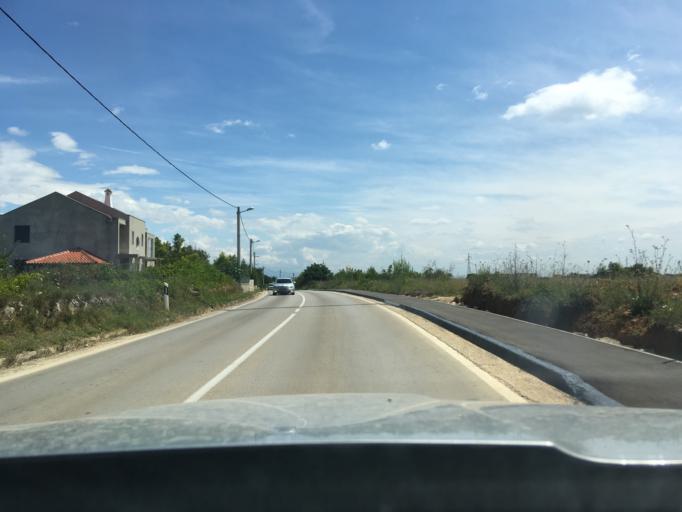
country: HR
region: Zadarska
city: Nin
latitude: 44.2465
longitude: 15.1580
